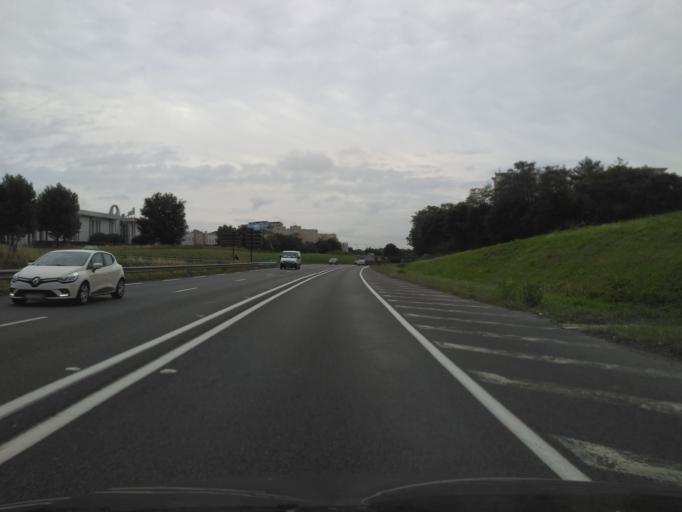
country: FR
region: Ile-de-France
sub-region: Departement de Seine-et-Marne
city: Rubelles
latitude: 48.5523
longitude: 2.6684
